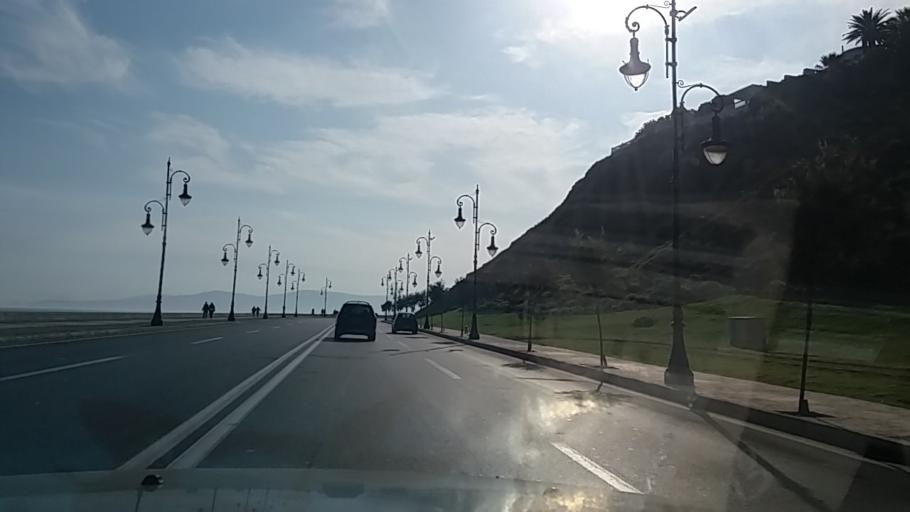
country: MA
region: Tanger-Tetouan
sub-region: Tanger-Assilah
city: Tangier
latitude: 35.7950
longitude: -5.8273
